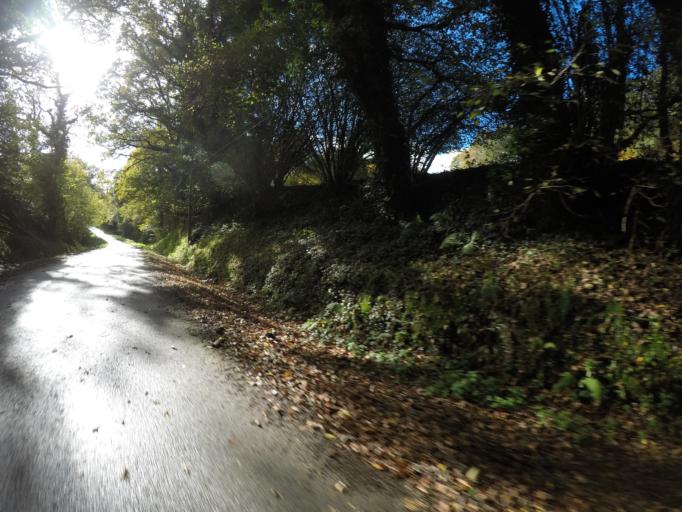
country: FR
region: Brittany
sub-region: Departement des Cotes-d'Armor
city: Callac
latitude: 48.4426
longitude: -3.3207
